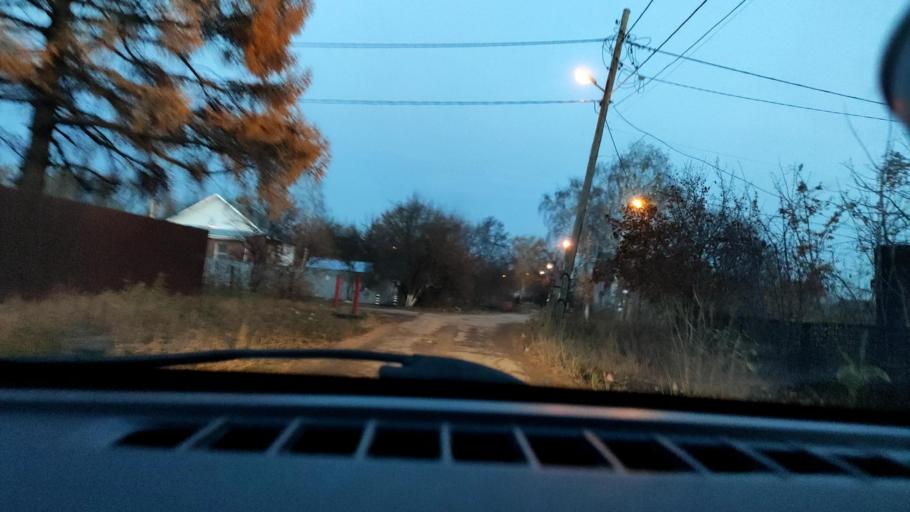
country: RU
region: Samara
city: Petra-Dubrava
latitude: 53.2628
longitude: 50.3344
